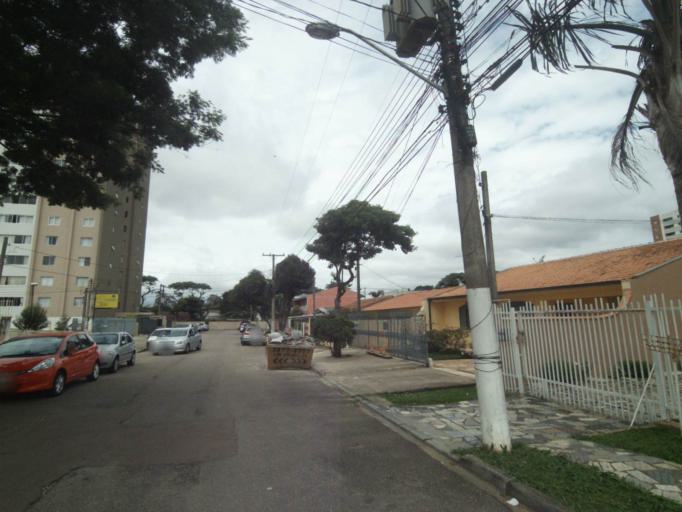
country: BR
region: Parana
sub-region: Curitiba
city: Curitiba
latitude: -25.4902
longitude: -49.2929
